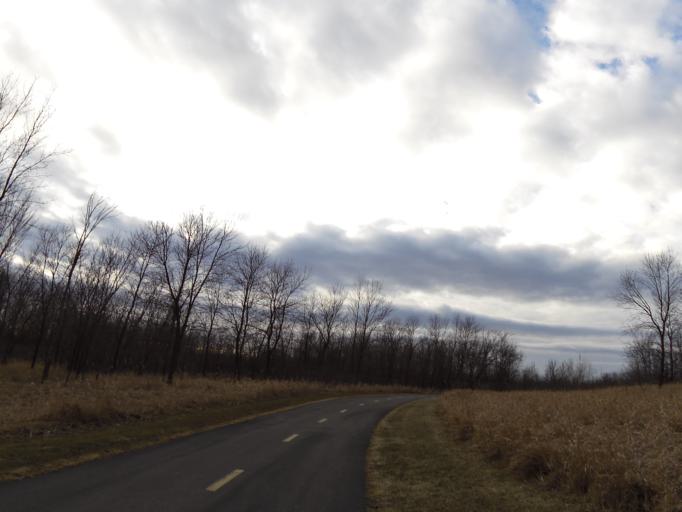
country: US
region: Minnesota
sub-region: Scott County
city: Prior Lake
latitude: 44.6975
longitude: -93.3920
